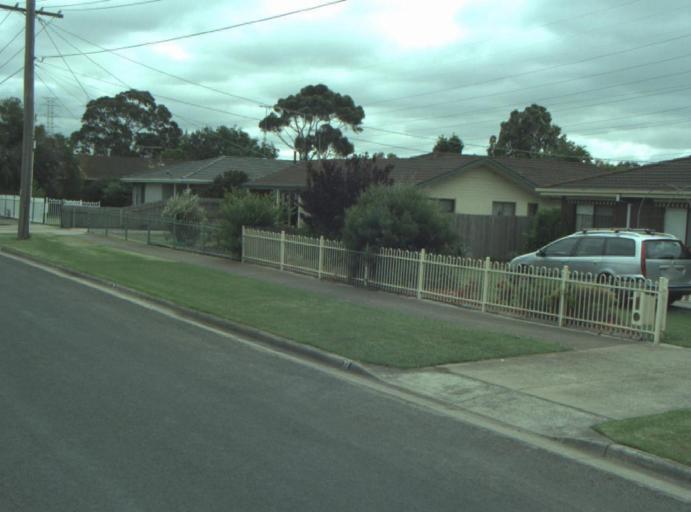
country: AU
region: Victoria
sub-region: Greater Geelong
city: Bell Post Hill
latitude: -38.0752
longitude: 144.3384
